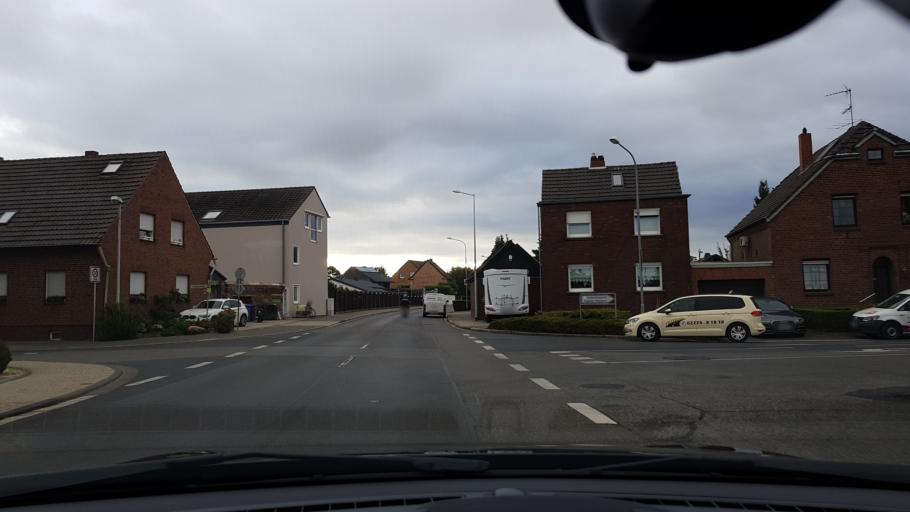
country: DE
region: North Rhine-Westphalia
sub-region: Regierungsbezirk Koln
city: Elsdorf
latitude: 50.9418
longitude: 6.5555
